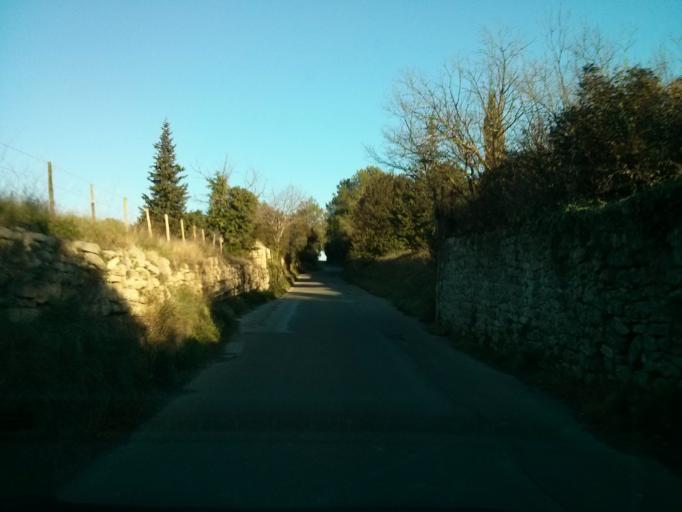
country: FR
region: Languedoc-Roussillon
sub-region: Departement du Gard
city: Aigues-Vives
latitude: 43.7397
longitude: 4.1880
